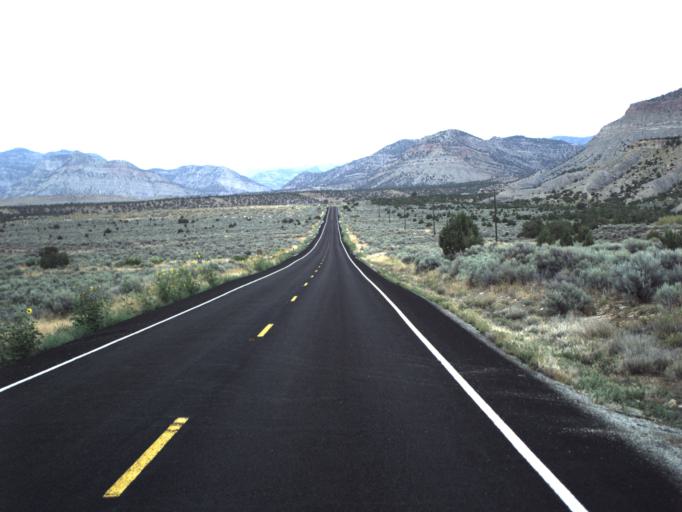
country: US
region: Utah
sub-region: Carbon County
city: East Carbon City
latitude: 39.5072
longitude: -110.3962
